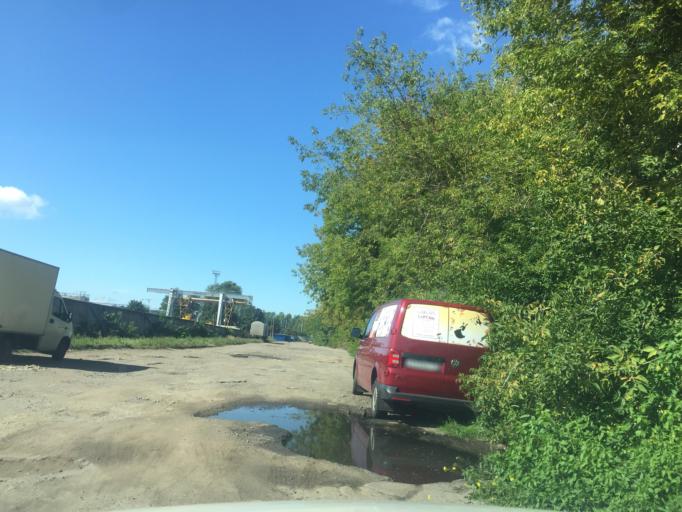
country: RU
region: St.-Petersburg
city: Kushelevka
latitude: 59.9915
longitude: 30.3588
